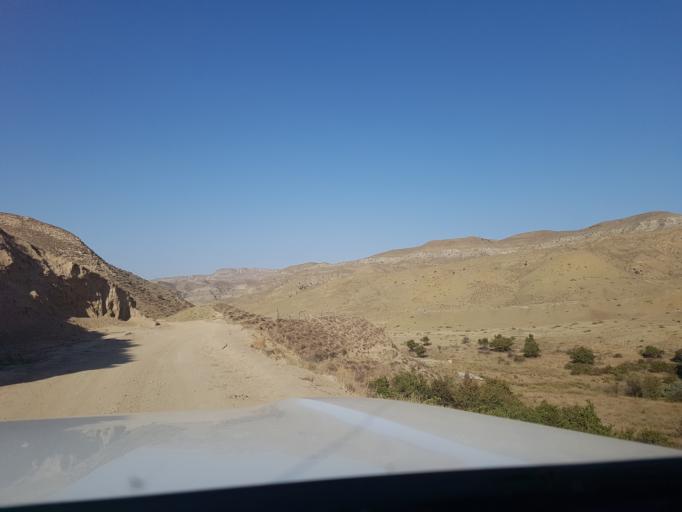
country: TM
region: Balkan
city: Magtymguly
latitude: 38.3016
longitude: 56.7713
